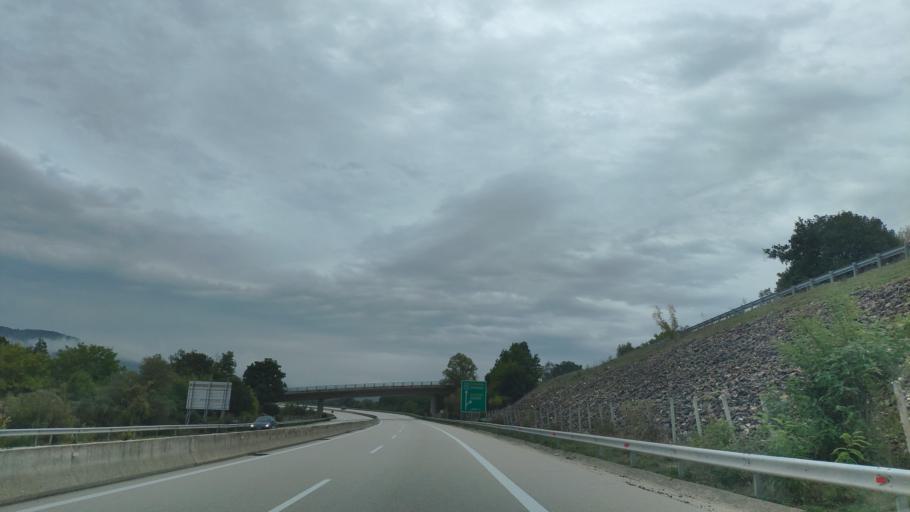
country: GR
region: Epirus
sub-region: Nomos Ioanninon
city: Pedini
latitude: 39.5553
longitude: 20.7639
